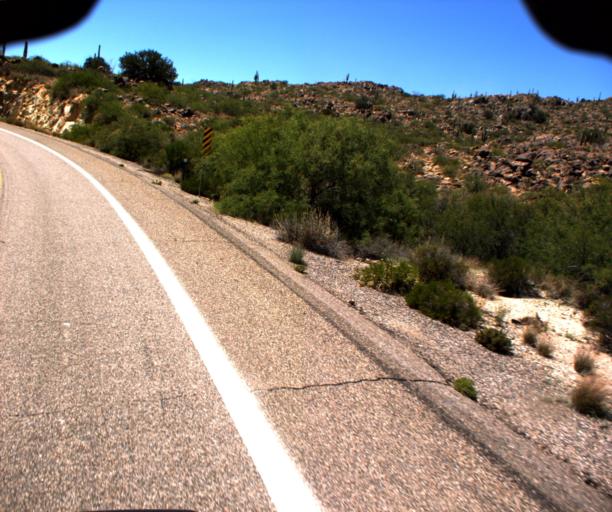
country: US
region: Arizona
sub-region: Yavapai County
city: Bagdad
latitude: 34.5249
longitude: -113.1234
